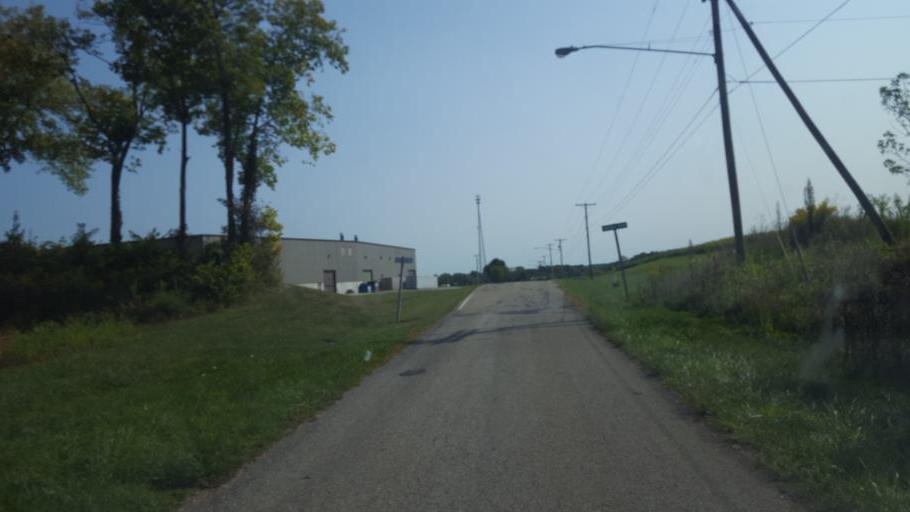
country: US
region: Ohio
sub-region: Knox County
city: Fredericktown
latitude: 40.4858
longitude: -82.5662
